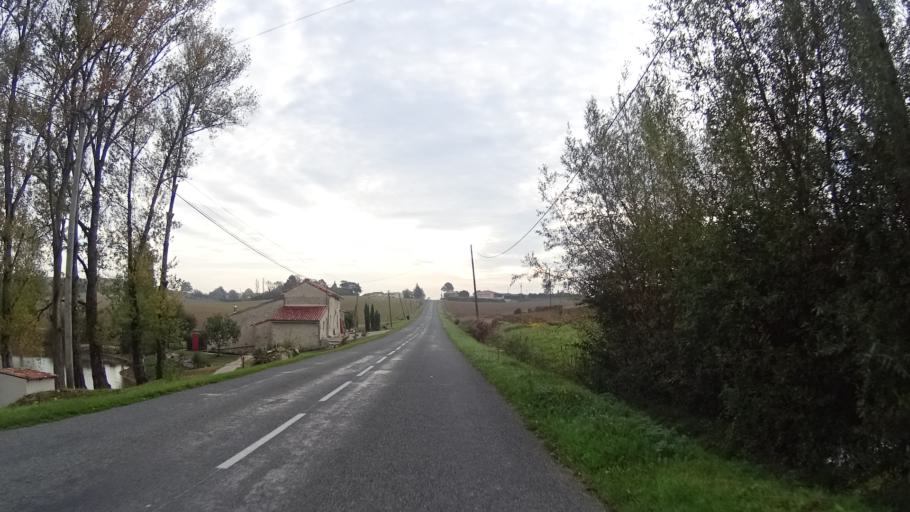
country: FR
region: Aquitaine
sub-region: Departement du Lot-et-Garonne
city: Laplume
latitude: 44.1004
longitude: 0.5575
